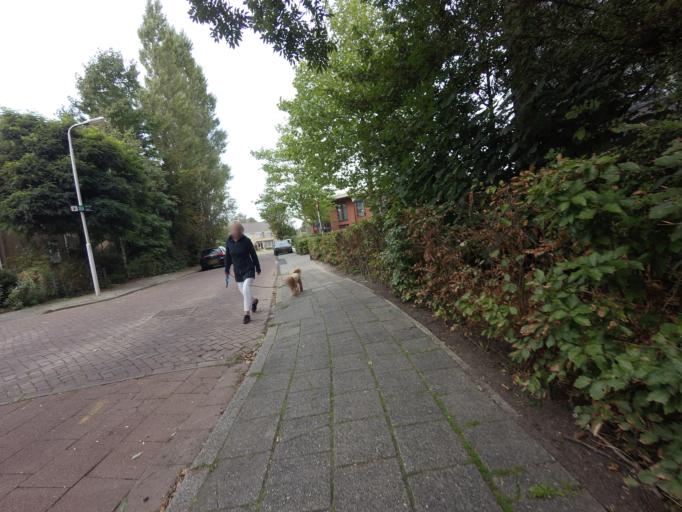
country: NL
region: Friesland
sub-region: Sudwest Fryslan
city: Sneek
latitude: 53.0331
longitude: 5.6502
